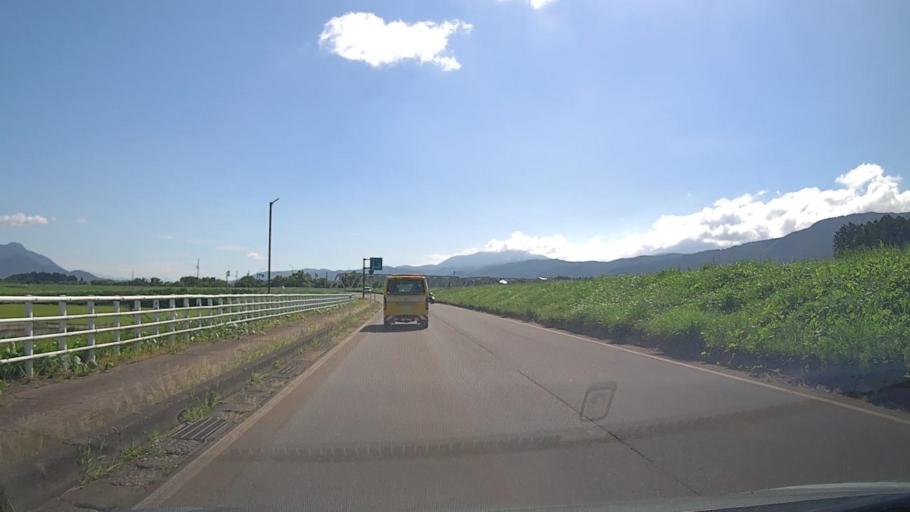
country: JP
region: Nagano
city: Iiyama
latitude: 36.9179
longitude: 138.4011
